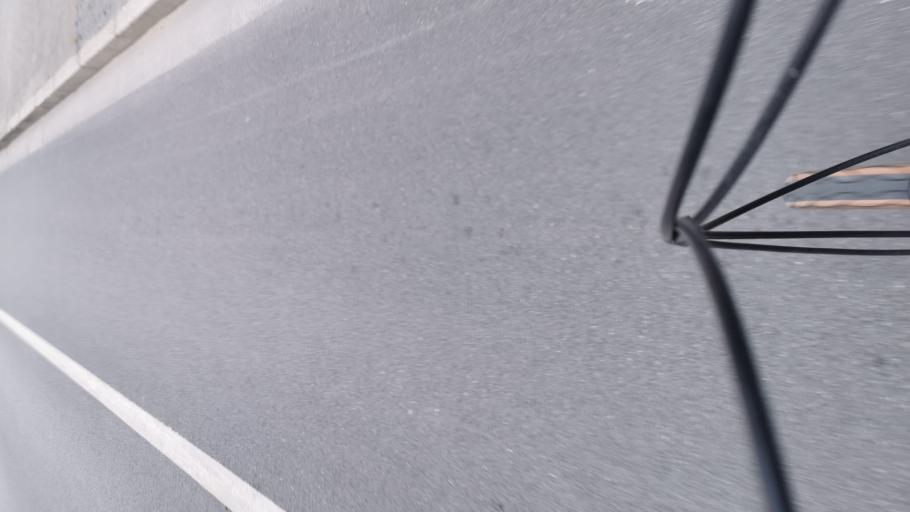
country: CN
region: Shanghai Shi
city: Changning
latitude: 31.2106
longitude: 121.3908
